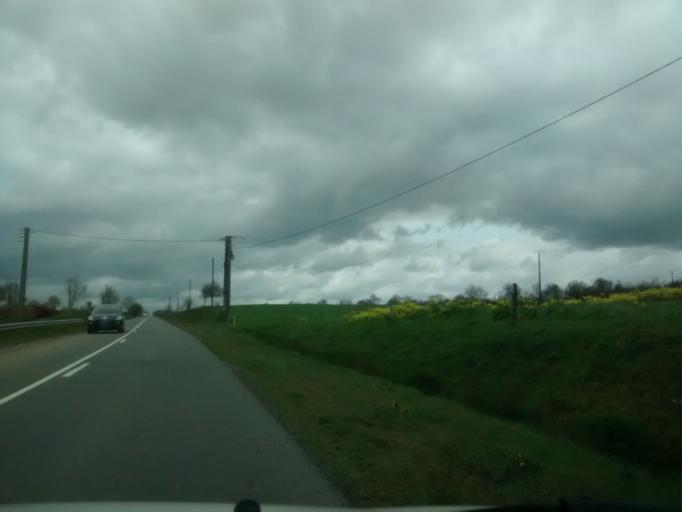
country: FR
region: Brittany
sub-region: Departement d'Ille-et-Vilaine
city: Livre-sur-Changeon
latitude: 48.2323
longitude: -1.3554
